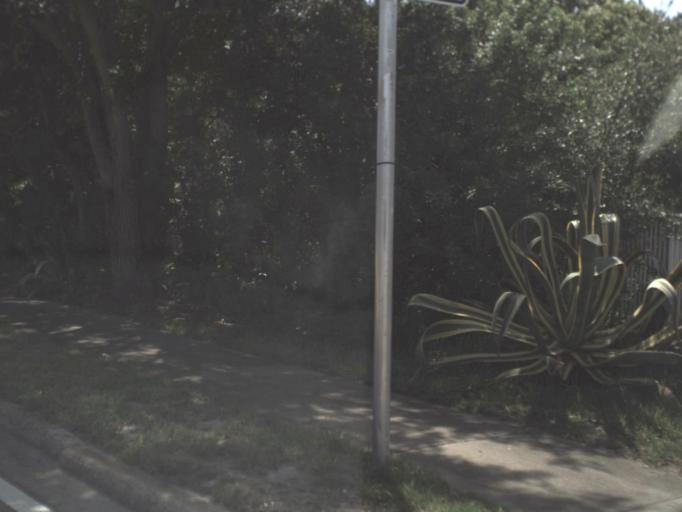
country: US
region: Florida
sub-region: Pinellas County
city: Dunedin
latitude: 28.0358
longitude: -82.7854
